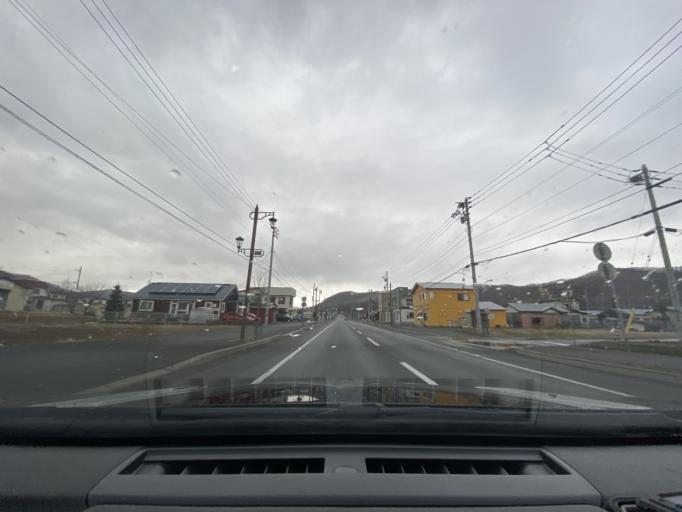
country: JP
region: Hokkaido
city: Otofuke
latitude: 43.2495
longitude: 143.5474
